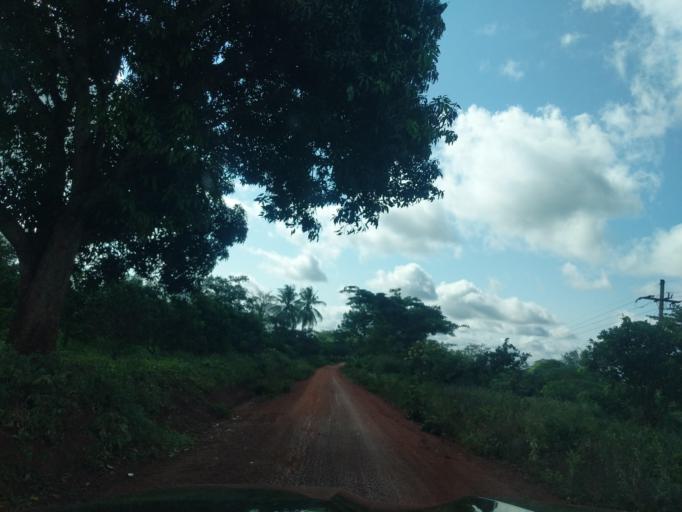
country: TZ
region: Tanga
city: Muheza
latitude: -5.4192
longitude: 38.6270
